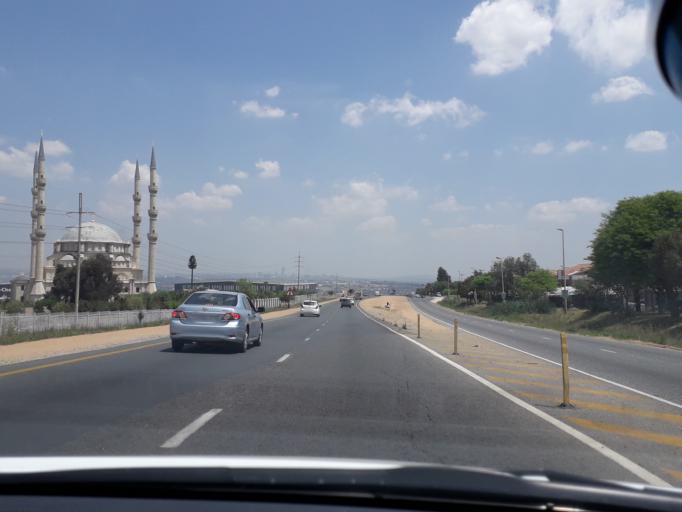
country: ZA
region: Gauteng
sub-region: City of Johannesburg Metropolitan Municipality
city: Midrand
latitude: -26.0117
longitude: 28.1305
